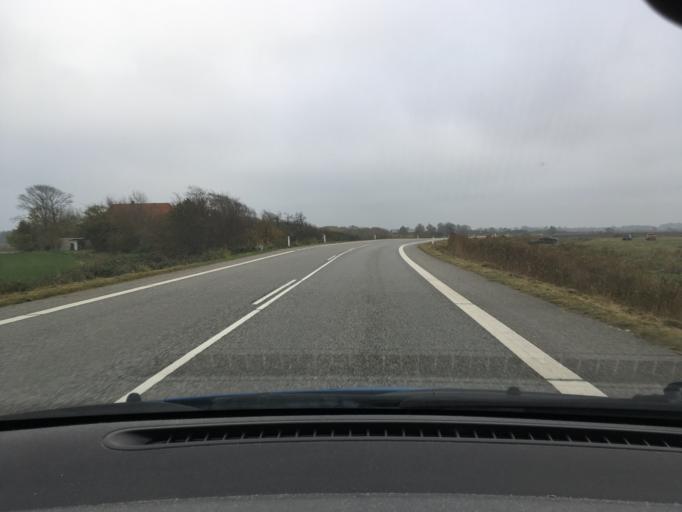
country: DE
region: Schleswig-Holstein
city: Aventoft
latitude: 54.9182
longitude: 8.8333
